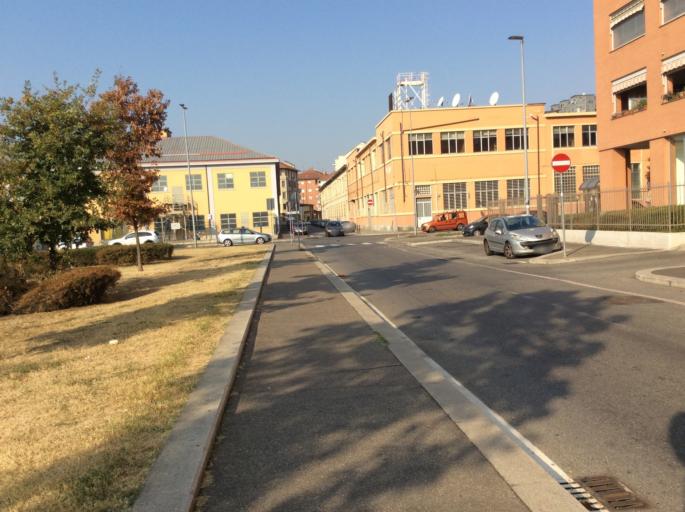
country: IT
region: Piedmont
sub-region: Provincia di Torino
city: Turin
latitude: 45.0916
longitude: 7.6835
